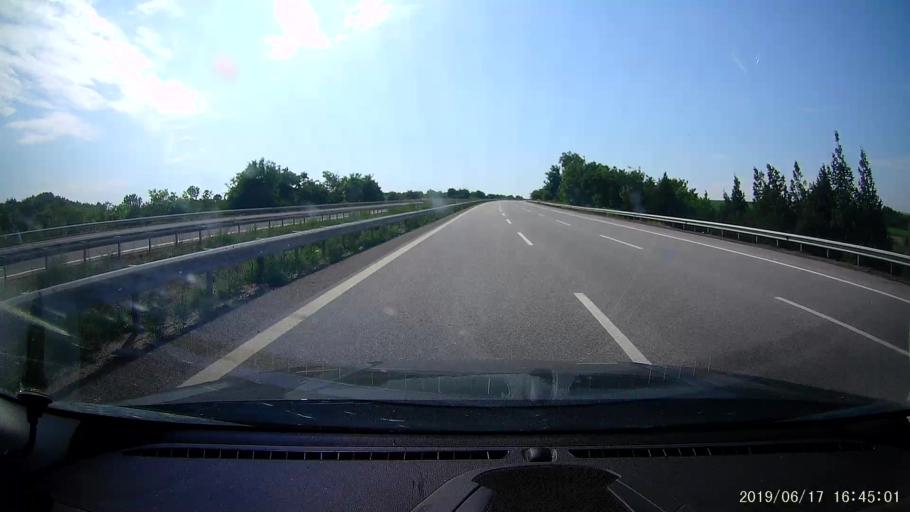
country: TR
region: Kirklareli
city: Luleburgaz
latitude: 41.4837
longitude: 27.2438
